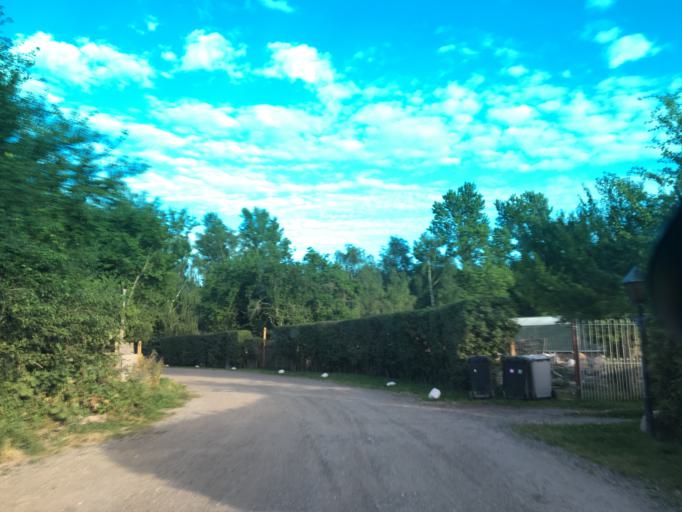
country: DK
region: Capital Region
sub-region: Tarnby Kommune
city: Tarnby
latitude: 55.5849
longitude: 12.5773
